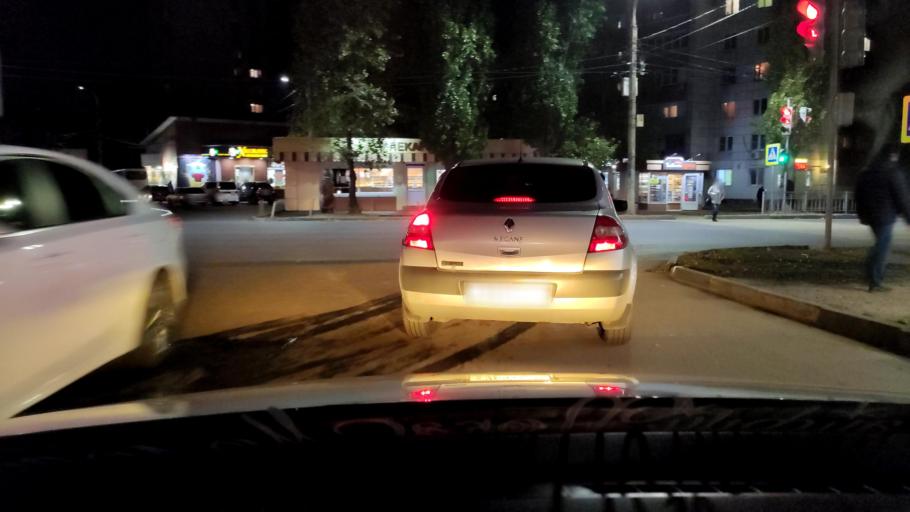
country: RU
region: Voronezj
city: Podgornoye
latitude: 51.7016
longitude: 39.1426
